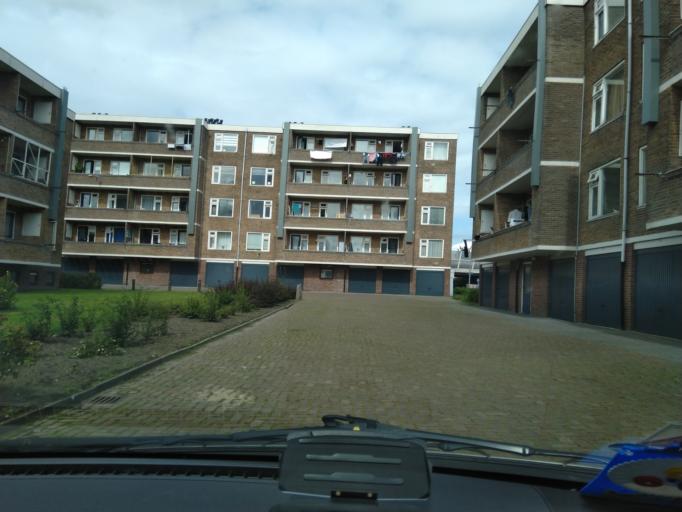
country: NL
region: Groningen
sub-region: Gemeente Groningen
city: Groningen
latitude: 53.2010
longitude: 6.5592
